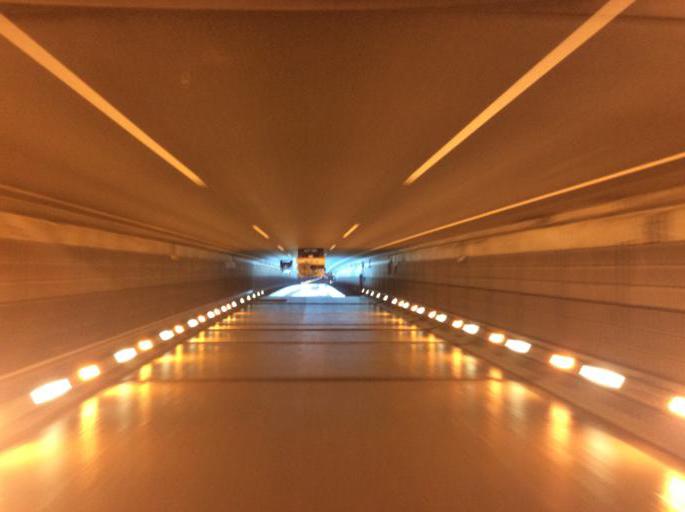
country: JP
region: Chiba
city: Nagareyama
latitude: 35.8983
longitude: 139.9235
